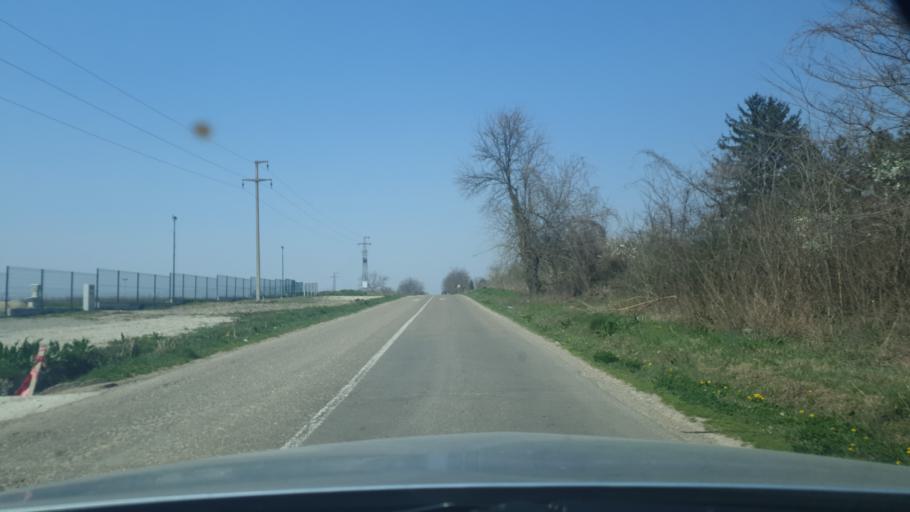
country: RS
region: Autonomna Pokrajina Vojvodina
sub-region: Sremski Okrug
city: Ruma
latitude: 45.0105
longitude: 19.7847
